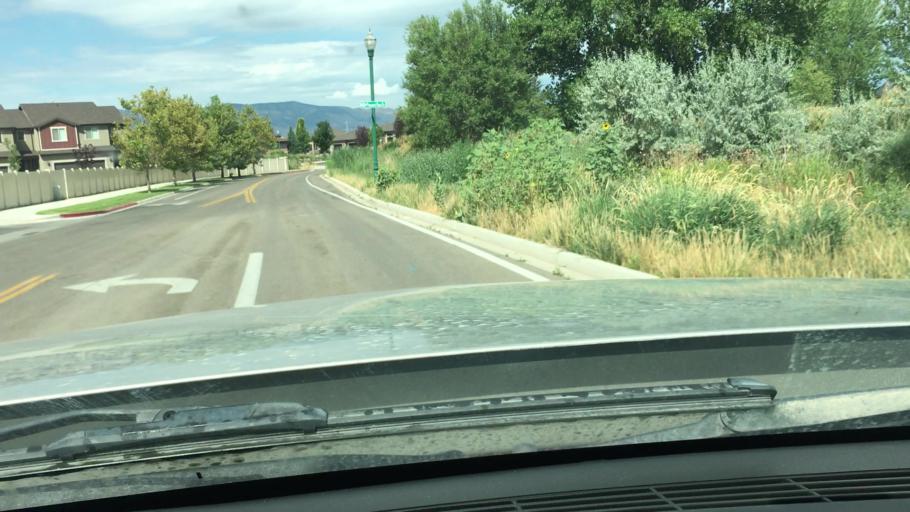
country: US
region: Utah
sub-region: Utah County
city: Orem
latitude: 40.2830
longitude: -111.7411
